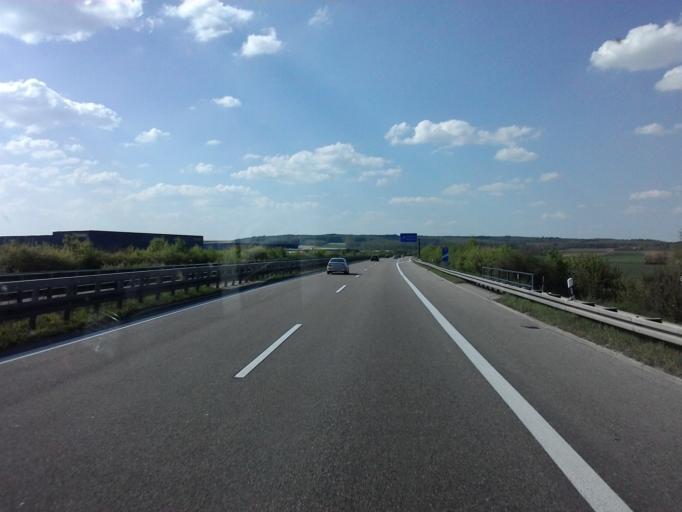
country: DE
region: Baden-Wuerttemberg
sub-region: Tuebingen Region
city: Langenau
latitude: 48.4879
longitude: 10.0937
